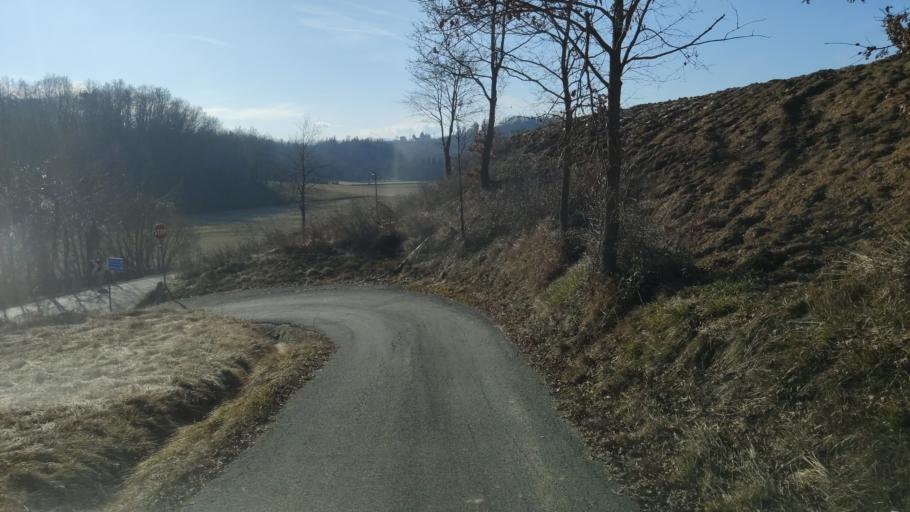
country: IT
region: Piedmont
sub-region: Provincia di Cuneo
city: Camerana
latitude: 44.4091
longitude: 8.1303
